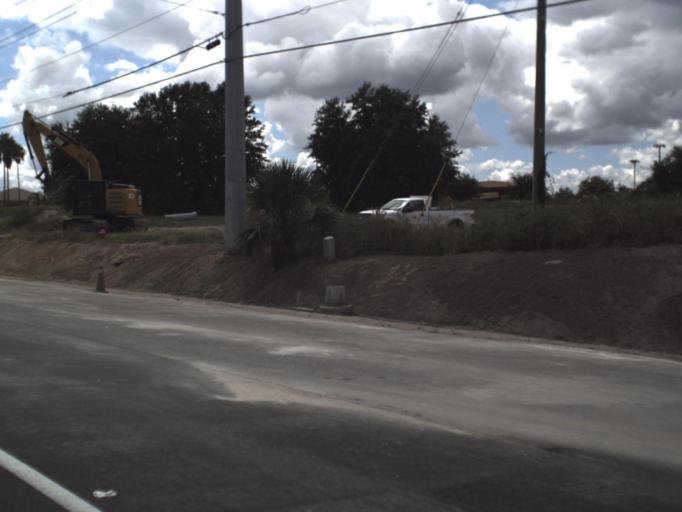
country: US
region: Florida
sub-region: Polk County
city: Highland City
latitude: 27.9825
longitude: -81.8900
